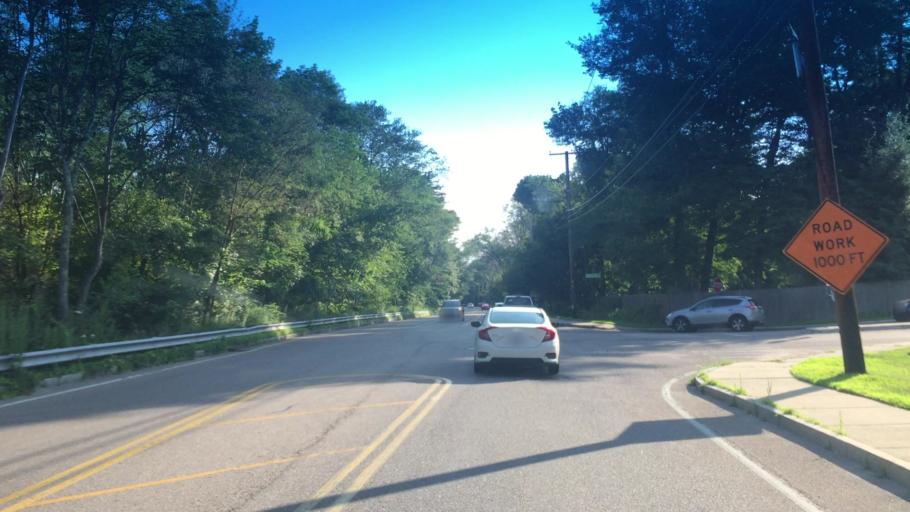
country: US
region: Massachusetts
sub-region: Norfolk County
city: Millis-Clicquot
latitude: 42.1780
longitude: -71.3329
